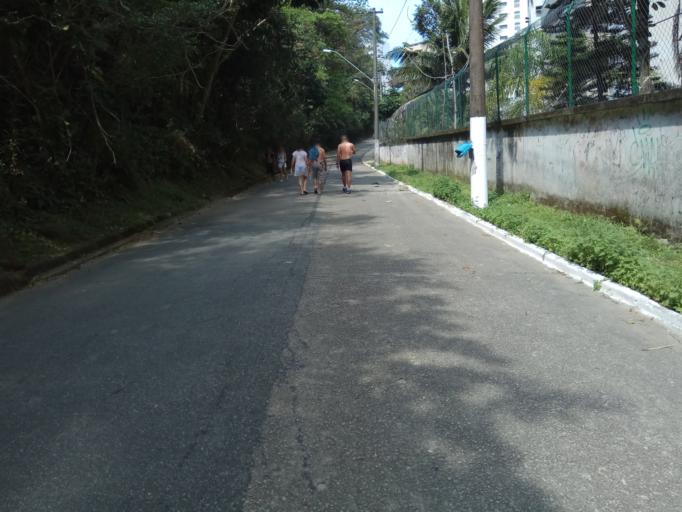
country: BR
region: Sao Paulo
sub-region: Guaruja
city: Guaruja
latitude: -23.9944
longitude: -46.2495
